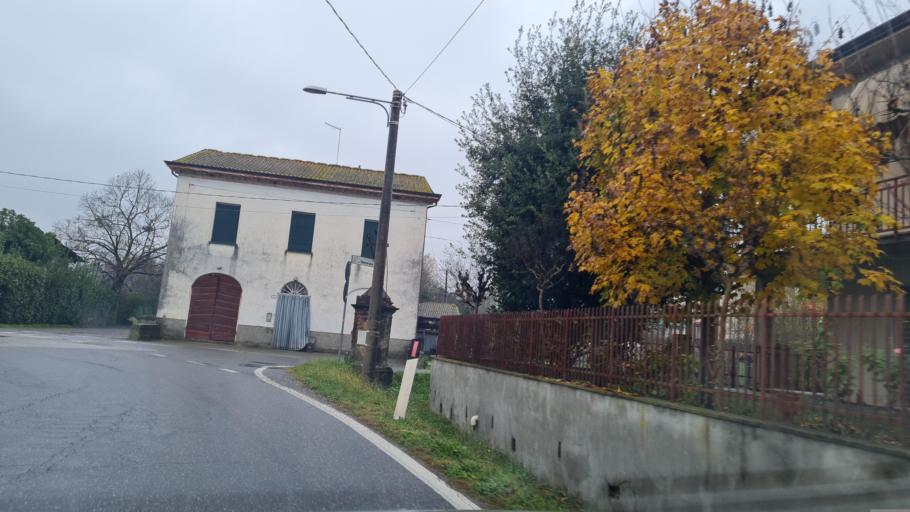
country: IT
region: Tuscany
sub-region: Provincia di Lucca
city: Lucca
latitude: 43.8588
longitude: 10.4514
